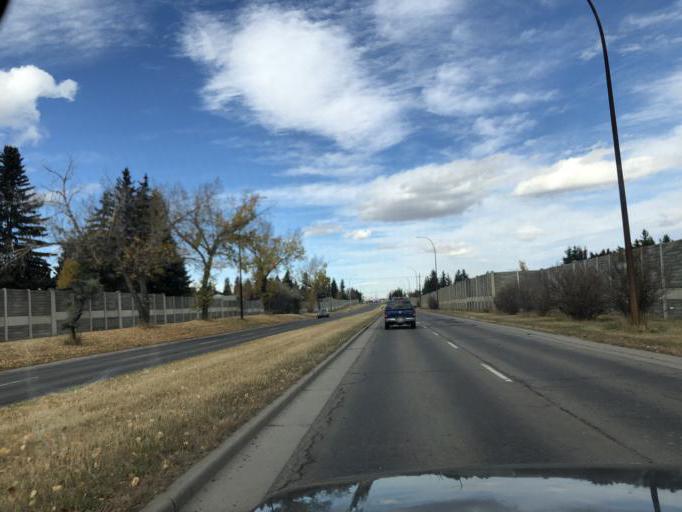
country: CA
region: Alberta
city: Calgary
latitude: 50.9555
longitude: -114.0947
